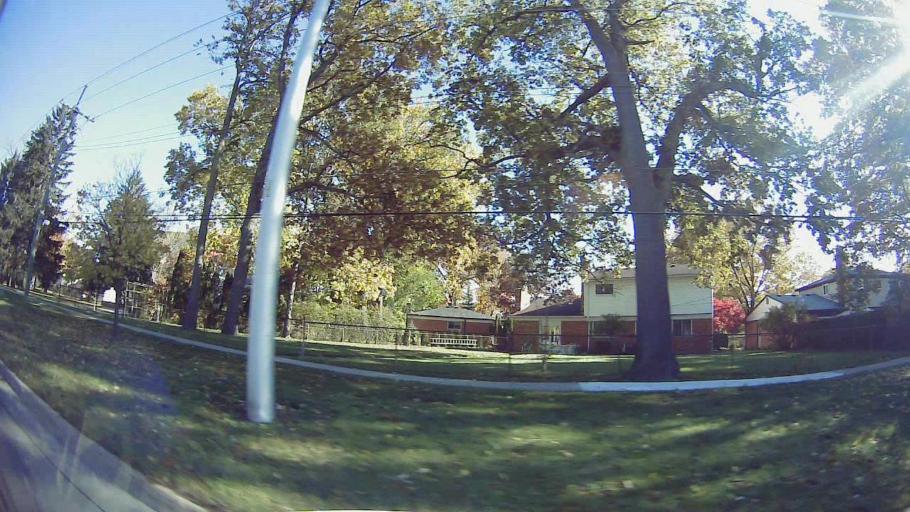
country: US
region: Michigan
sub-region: Oakland County
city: Farmington
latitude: 42.4489
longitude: -83.3756
